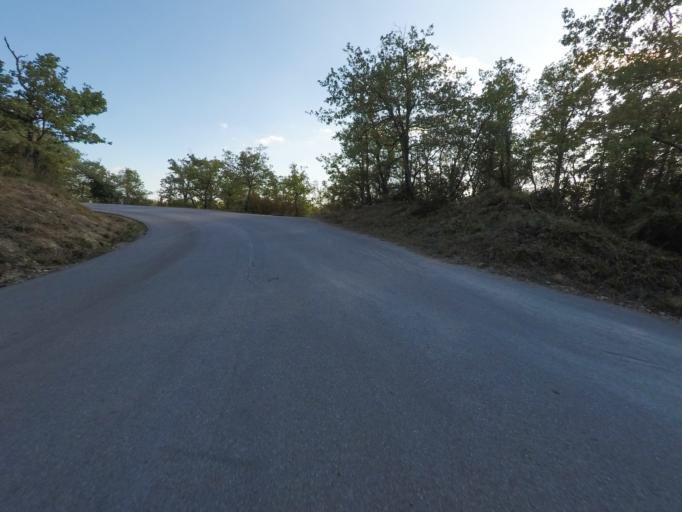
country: IT
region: Tuscany
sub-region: Provincia di Siena
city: Radda in Chianti
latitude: 43.4547
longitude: 11.3834
